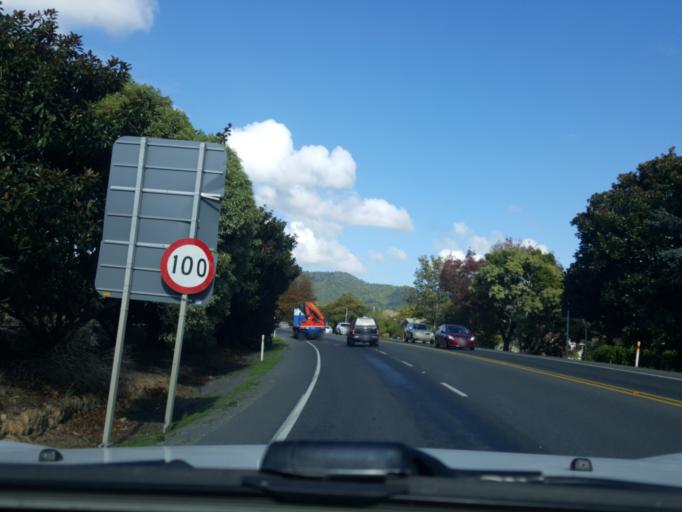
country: NZ
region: Waikato
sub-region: Waikato District
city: Ngaruawahia
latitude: -37.5807
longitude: 175.1591
